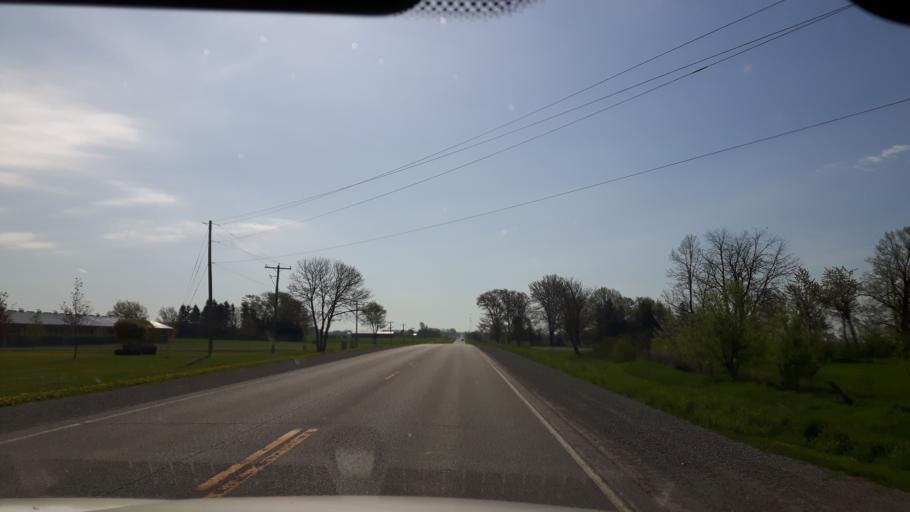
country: CA
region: Ontario
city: Bluewater
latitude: 43.5309
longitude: -81.5860
